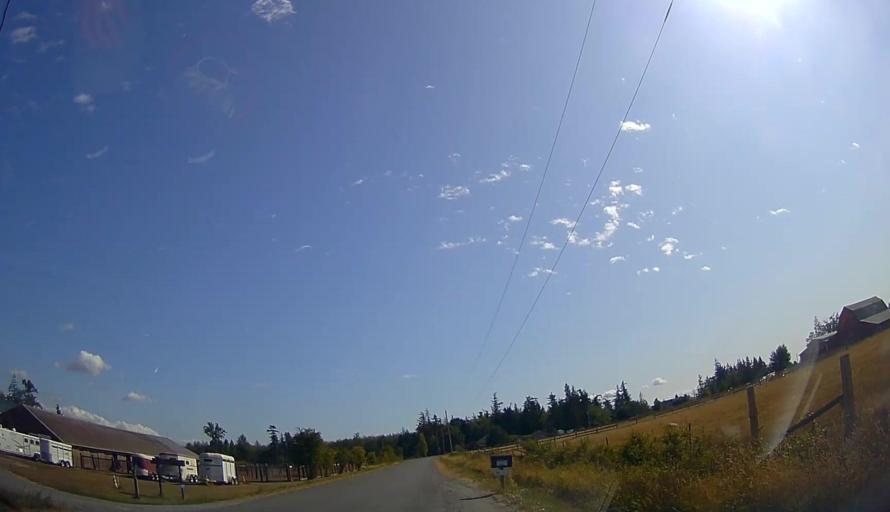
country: US
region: Washington
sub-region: Skagit County
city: Burlington
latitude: 48.4958
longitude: -122.4610
